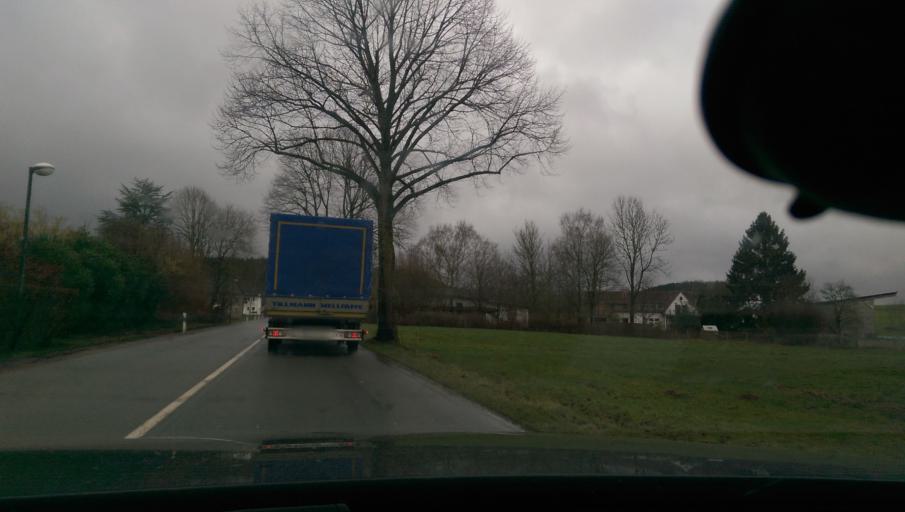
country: DE
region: North Rhine-Westphalia
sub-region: Regierungsbezirk Arnsberg
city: Sundern
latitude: 51.2979
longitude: 7.9842
